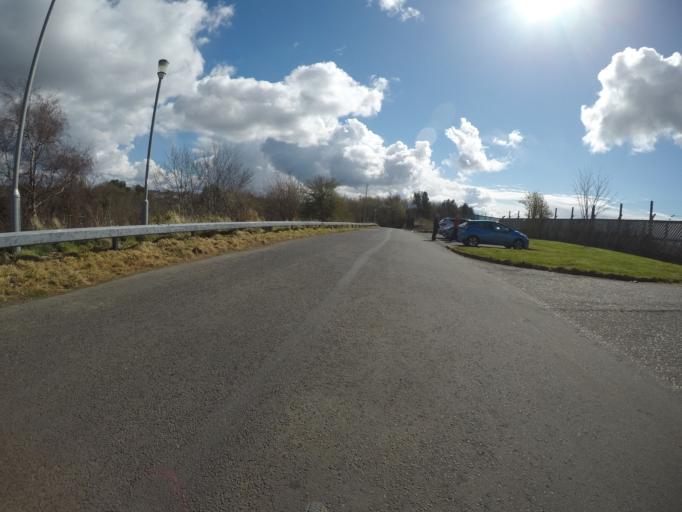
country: GB
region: Scotland
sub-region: North Ayrshire
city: Kilwinning
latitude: 55.6533
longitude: -4.6949
